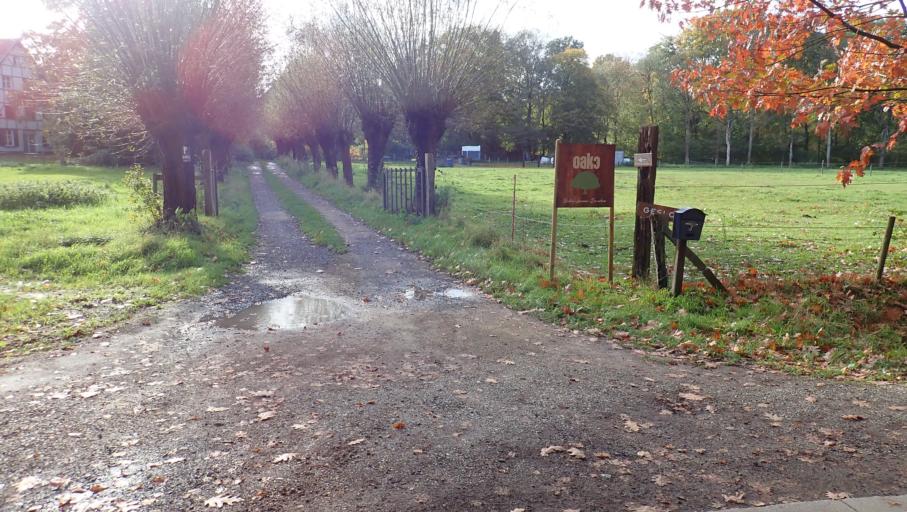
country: BE
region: Flanders
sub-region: Provincie Antwerpen
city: Zoersel
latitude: 51.2599
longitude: 4.7026
